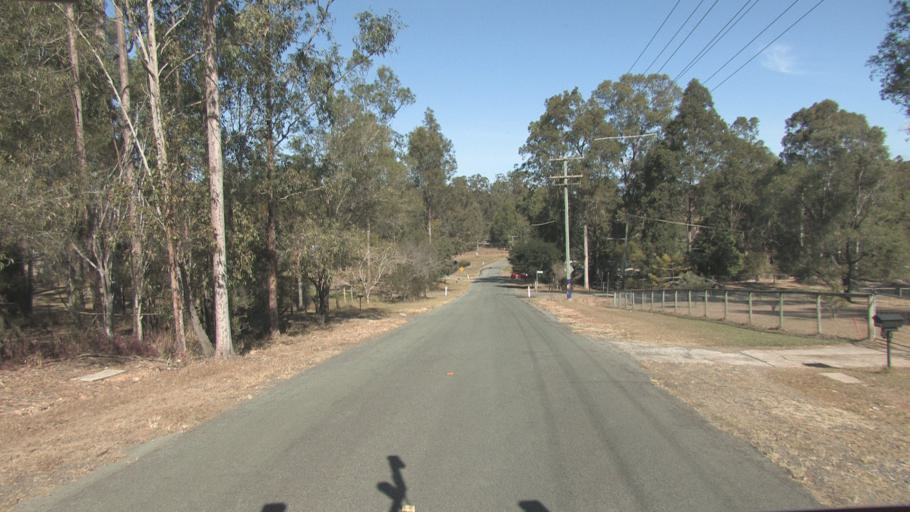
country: AU
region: Queensland
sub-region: Logan
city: Cedar Vale
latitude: -27.8555
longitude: 152.9850
